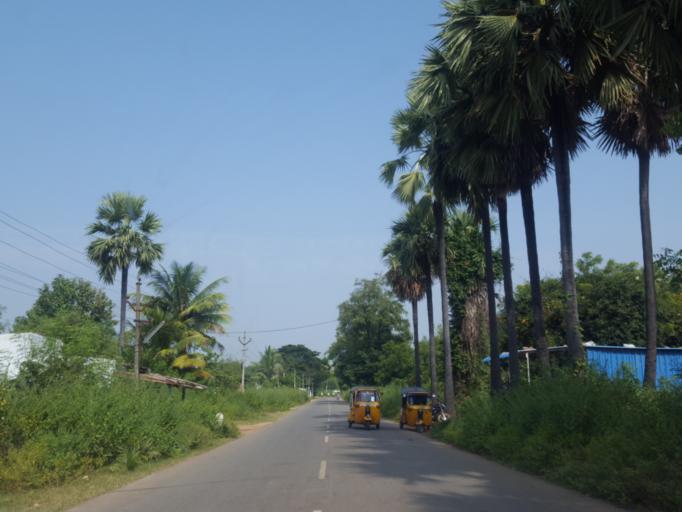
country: IN
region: Telangana
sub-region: Khammam
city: Yellandu
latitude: 17.6108
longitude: 80.3124
